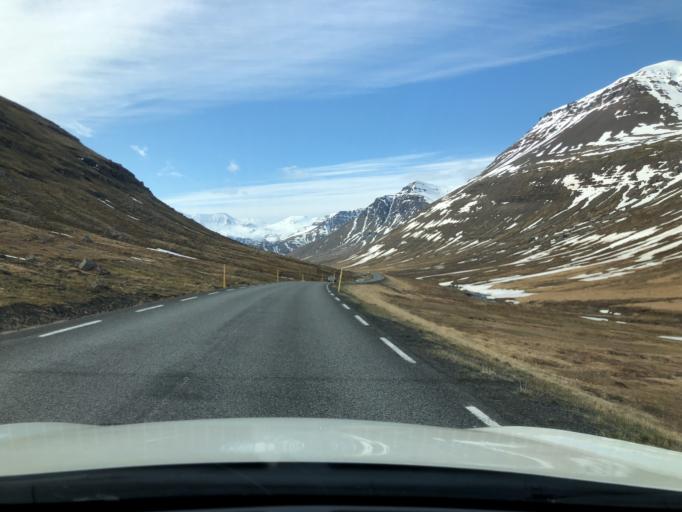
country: IS
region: East
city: Reydarfjoerdur
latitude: 65.0753
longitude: -14.3388
